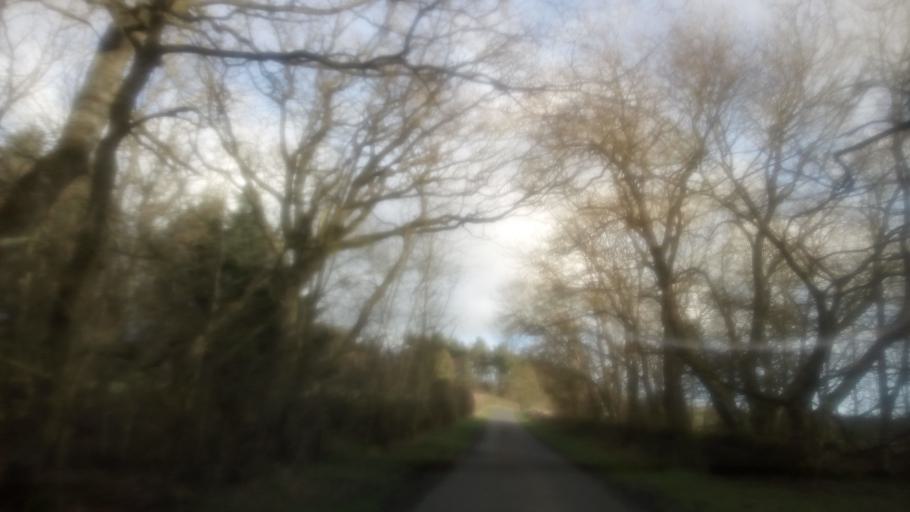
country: GB
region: Scotland
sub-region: The Scottish Borders
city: Jedburgh
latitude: 55.4723
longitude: -2.6110
